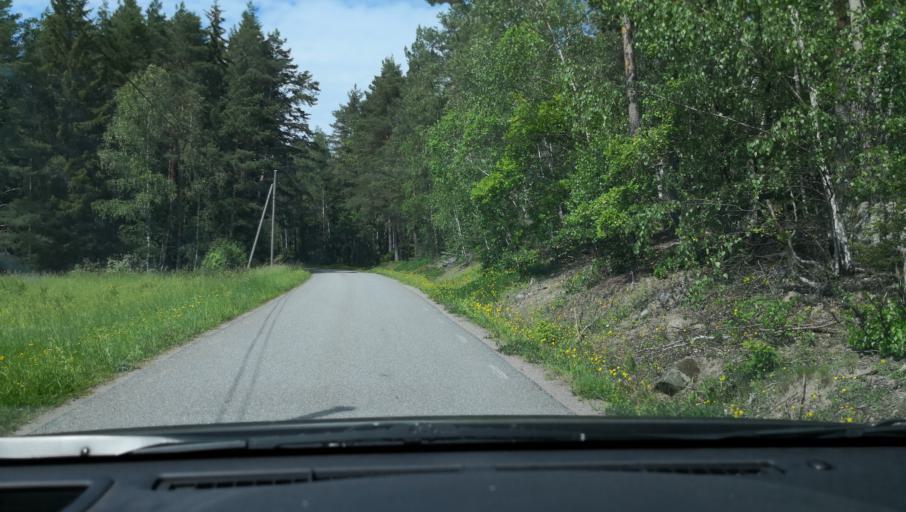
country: SE
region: Stockholm
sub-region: Sigtuna Kommun
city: Sigtuna
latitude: 59.6919
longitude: 17.6466
